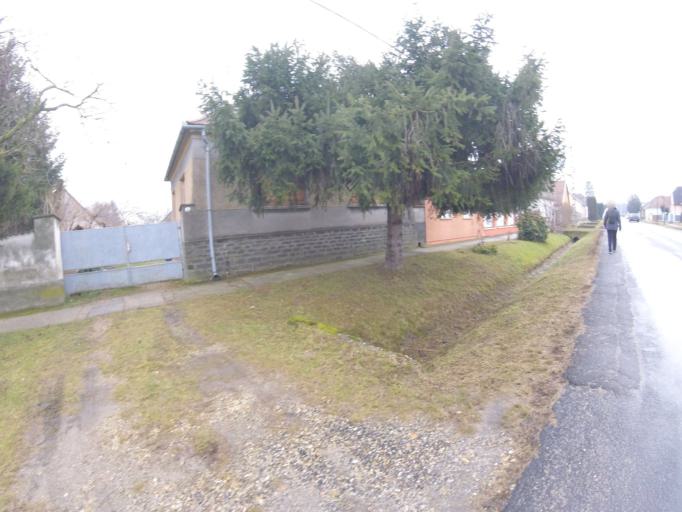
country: HU
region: Vas
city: Sarvar
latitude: 47.2449
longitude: 17.0303
